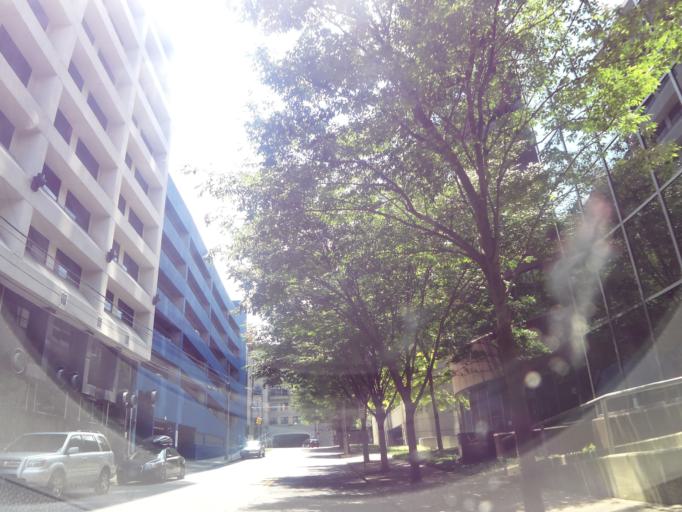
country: US
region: Tennessee
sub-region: Davidson County
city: Nashville
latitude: 36.1531
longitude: -86.7957
